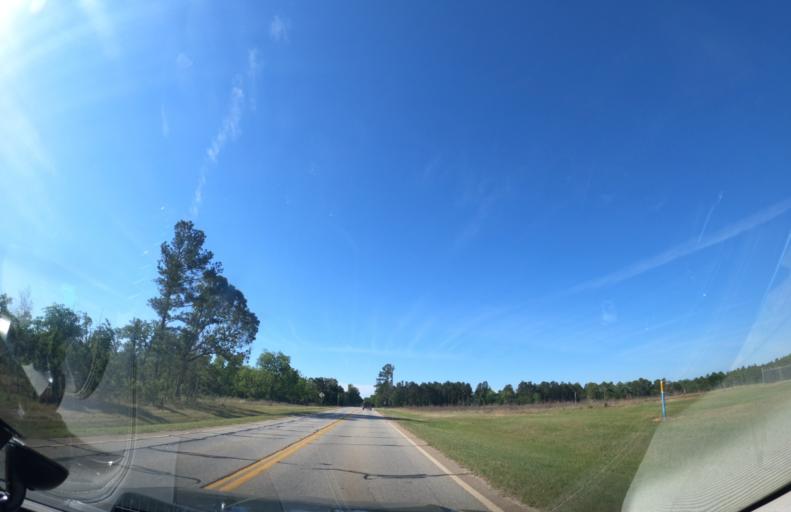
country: US
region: Georgia
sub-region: Jefferson County
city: Wrens
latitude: 33.2530
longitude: -82.3870
